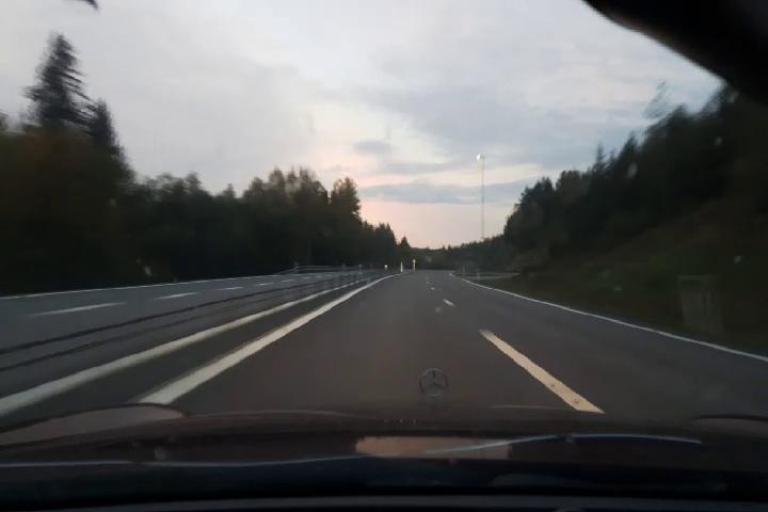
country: SE
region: Vaesternorrland
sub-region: Kramfors Kommun
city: Nordingra
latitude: 62.9415
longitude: 18.0945
